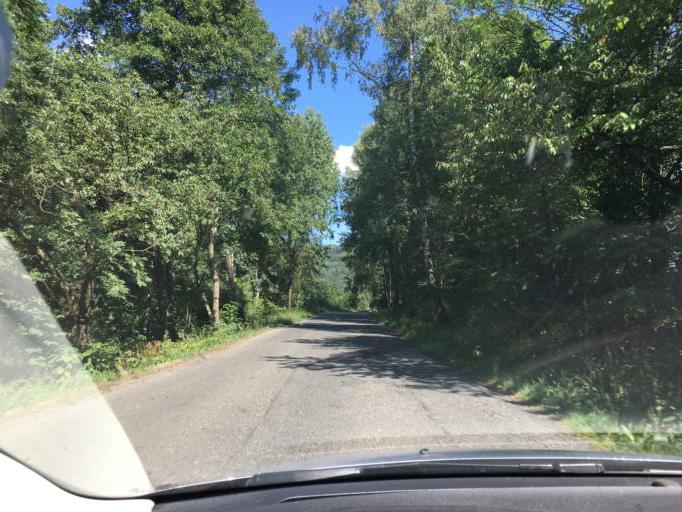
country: CZ
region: Liberecky
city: Mala Skala
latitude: 50.6539
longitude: 15.1439
